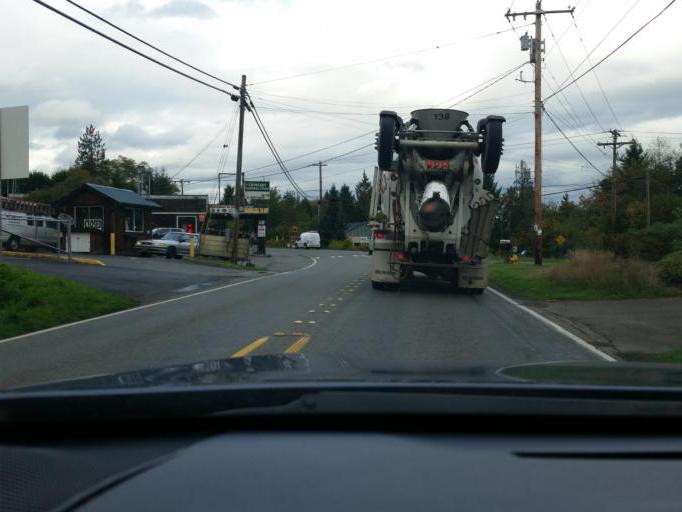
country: US
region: Washington
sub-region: Snohomish County
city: Cathcart
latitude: 47.8474
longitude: -122.0998
